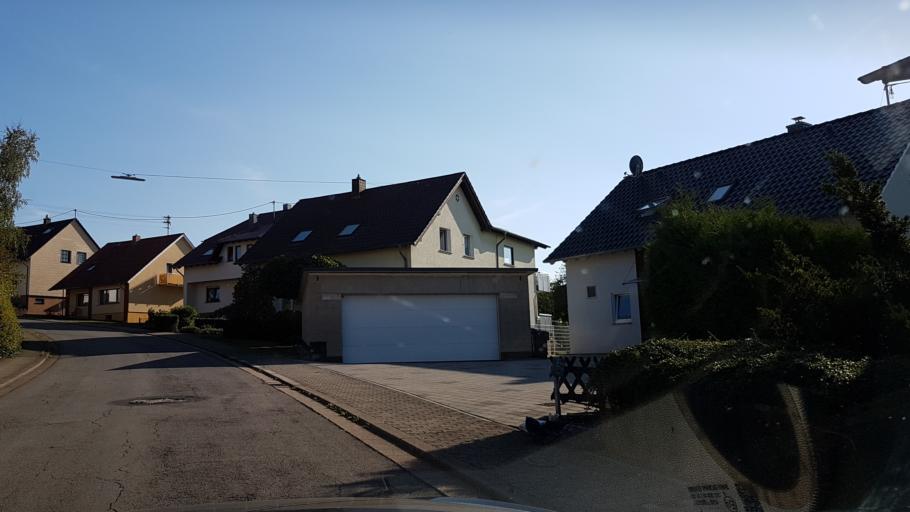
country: DE
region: Saarland
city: Eppelborn
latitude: 49.3922
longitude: 7.0049
